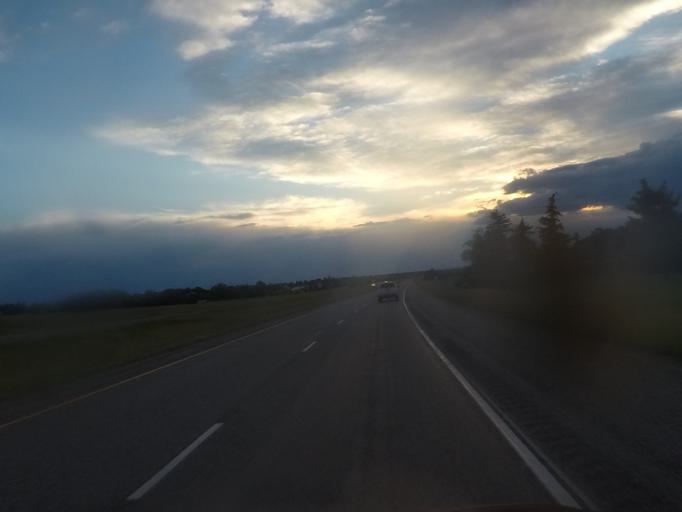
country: US
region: Montana
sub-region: Gallatin County
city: Bozeman
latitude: 45.6645
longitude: -110.9725
